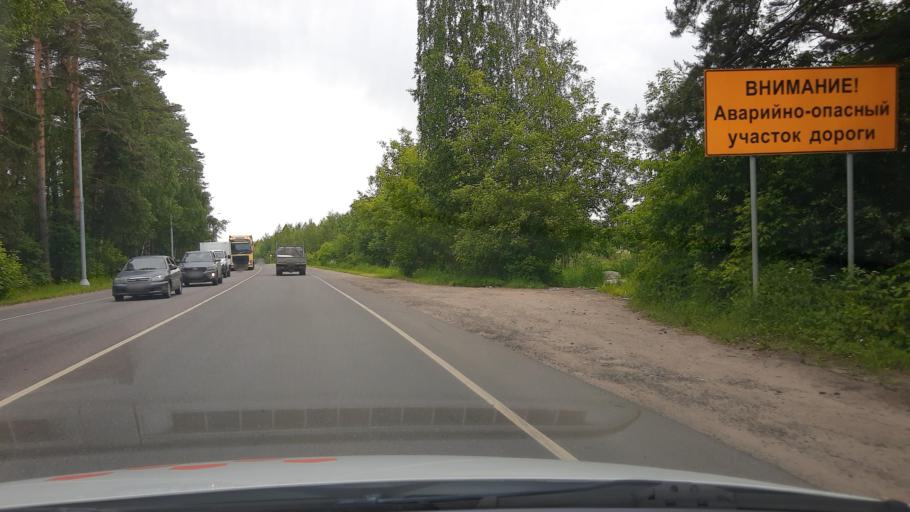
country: RU
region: Moskovskaya
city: Noginsk
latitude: 55.8682
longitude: 38.4223
